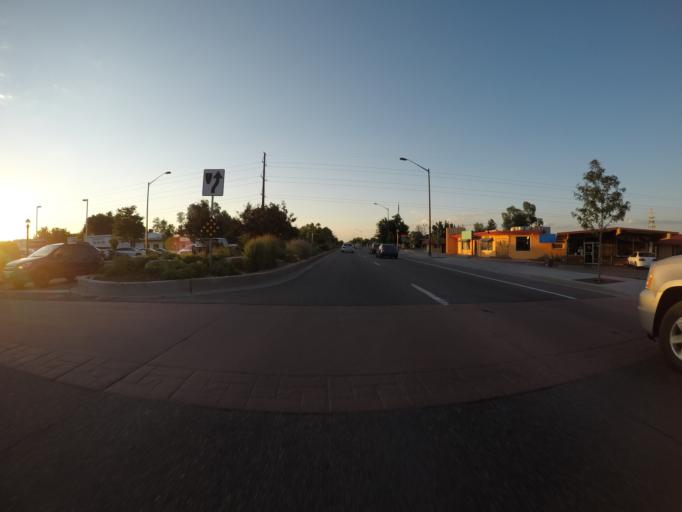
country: US
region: Colorado
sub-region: Larimer County
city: Fort Collins
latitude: 40.6037
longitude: -105.0765
